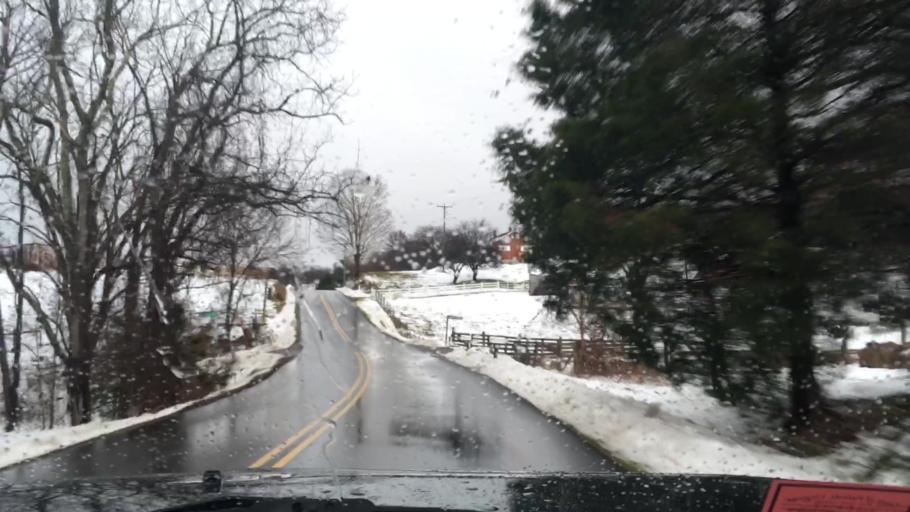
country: US
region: Virginia
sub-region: Pulaski County
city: Dublin
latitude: 37.0125
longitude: -80.6511
